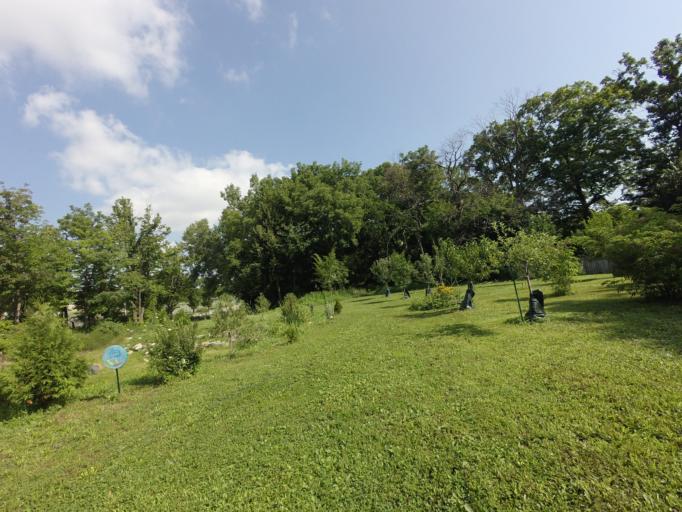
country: US
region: Wisconsin
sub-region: Milwaukee County
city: Saint Francis
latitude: 42.9771
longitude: -87.9189
